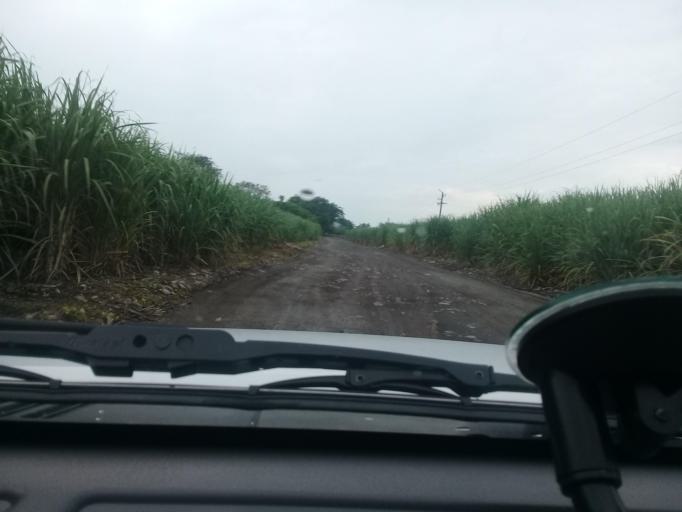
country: MX
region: Veracruz
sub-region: Puente Nacional
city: Cabezas
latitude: 19.3612
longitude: -96.4230
